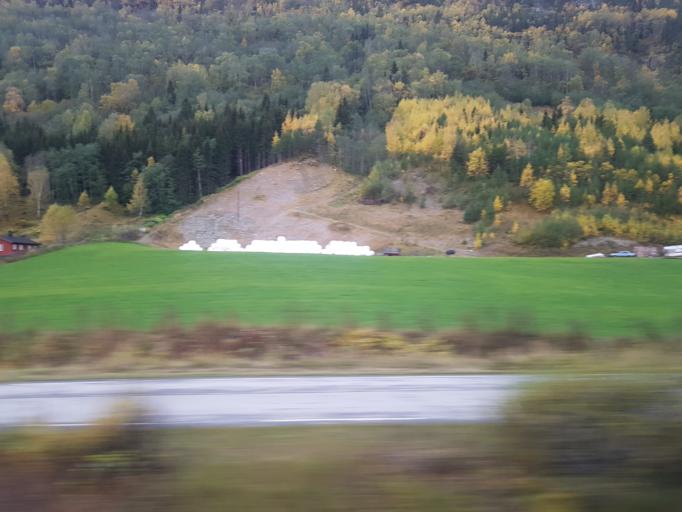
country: NO
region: Oppland
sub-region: Sel
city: Otta
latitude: 61.7812
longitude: 9.5335
